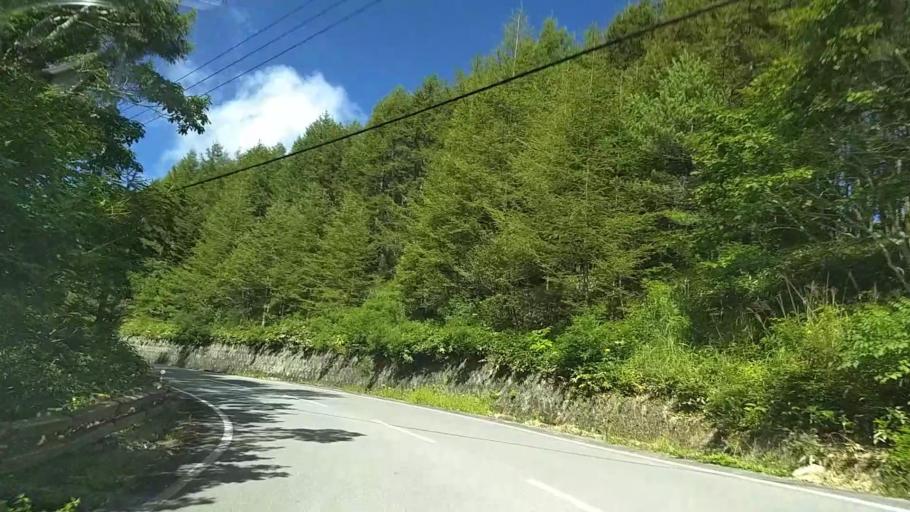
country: JP
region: Nagano
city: Suwa
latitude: 36.1119
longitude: 138.1702
